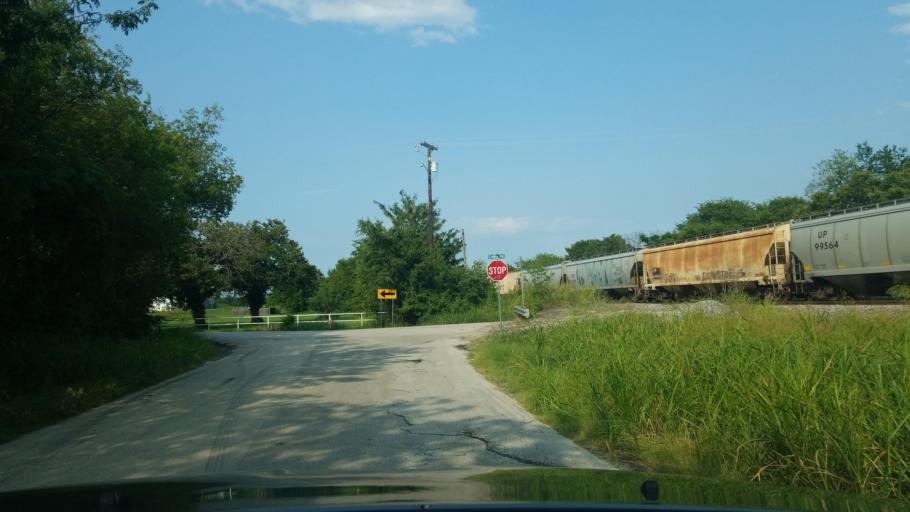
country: US
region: Texas
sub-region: Denton County
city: Cross Roads
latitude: 33.2468
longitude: -97.0621
